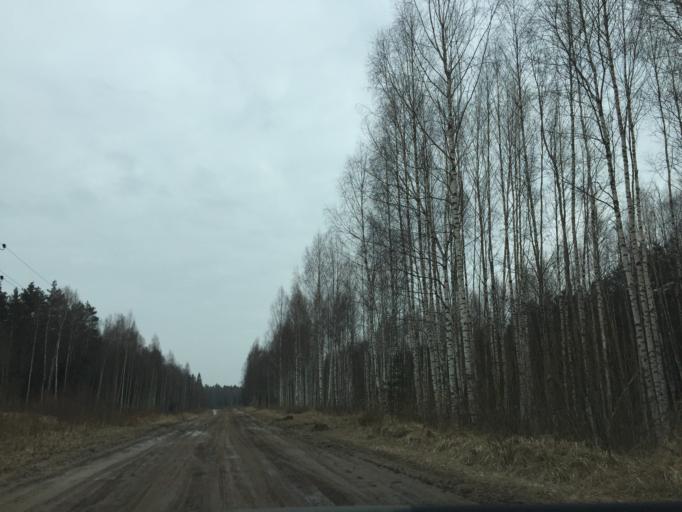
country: LV
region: Kekava
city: Balozi
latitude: 56.7866
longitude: 24.1289
